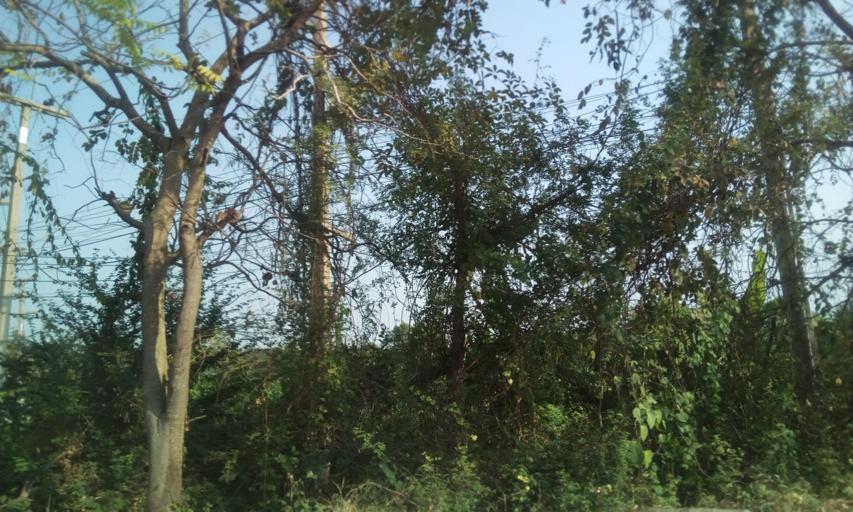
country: TH
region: Sing Buri
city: Sing Buri
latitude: 14.8708
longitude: 100.4015
